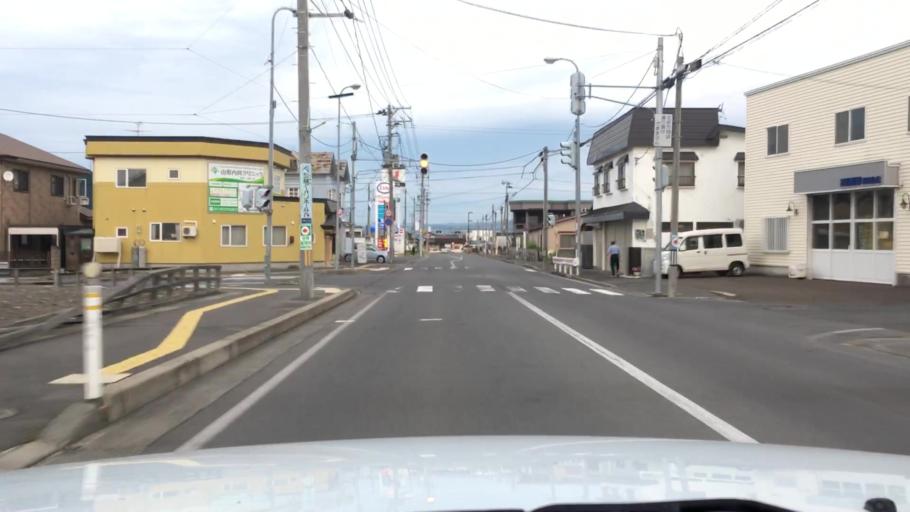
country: JP
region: Aomori
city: Hirosaki
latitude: 40.5909
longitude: 140.4857
